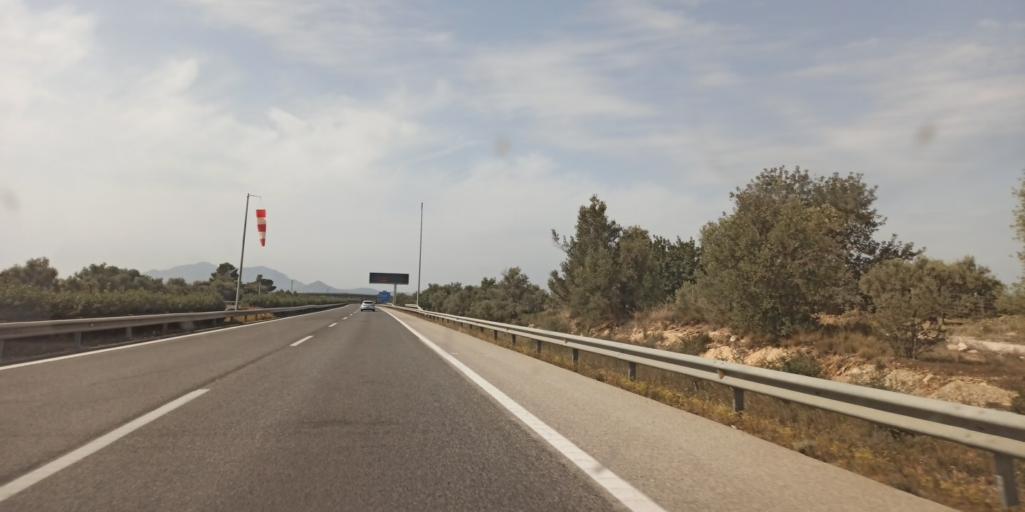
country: ES
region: Catalonia
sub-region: Provincia de Tarragona
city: Camarles
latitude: 40.7742
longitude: 0.6384
